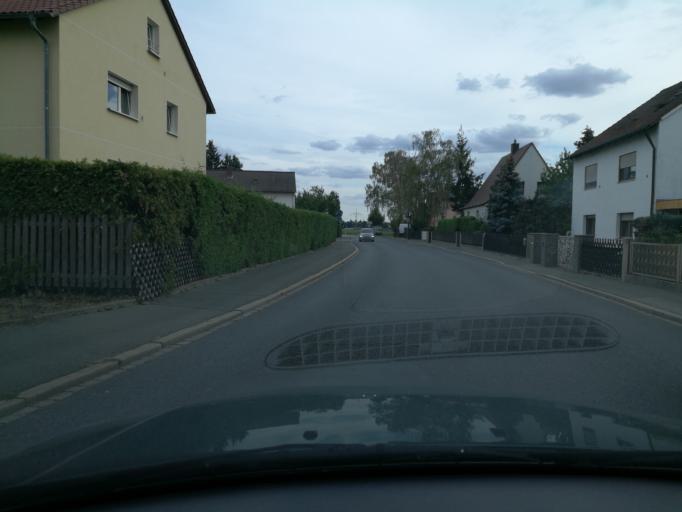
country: DE
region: Bavaria
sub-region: Regierungsbezirk Mittelfranken
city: Furth
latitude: 49.5074
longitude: 11.0046
